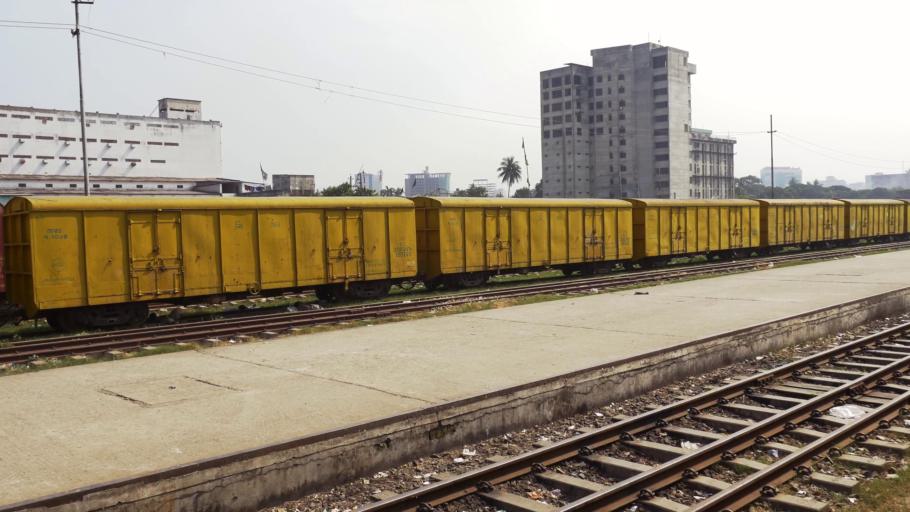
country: BD
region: Dhaka
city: Paltan
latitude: 23.7713
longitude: 90.3967
